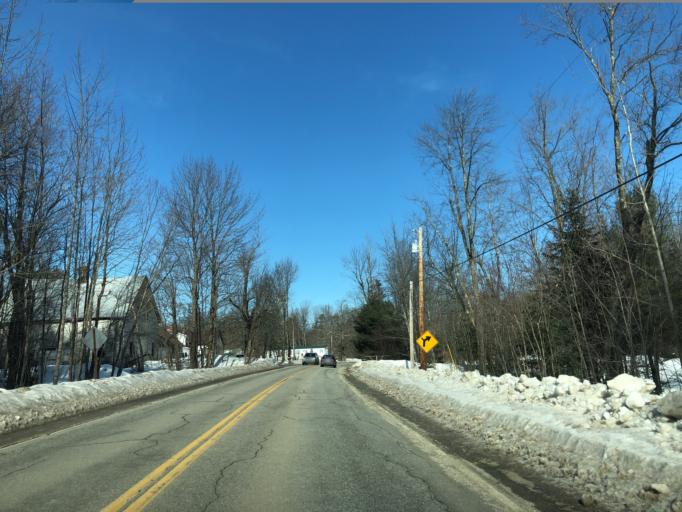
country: US
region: Maine
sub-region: Oxford County
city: Buckfield
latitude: 44.2284
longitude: -70.3396
